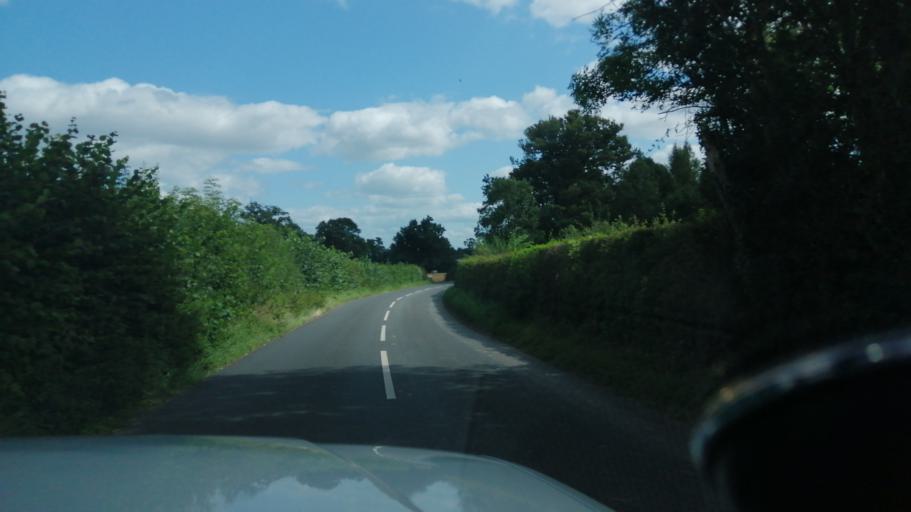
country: GB
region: England
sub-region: Herefordshire
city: Moccas
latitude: 52.0761
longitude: -2.9375
